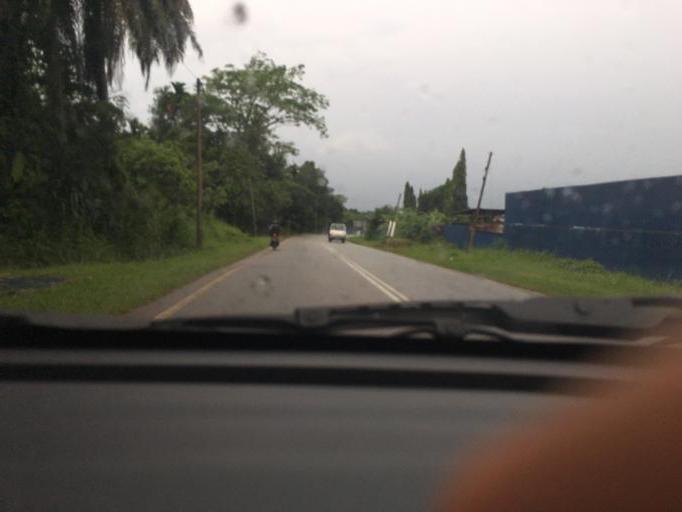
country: MY
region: Kedah
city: Bedong
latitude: 5.7009
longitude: 100.6326
